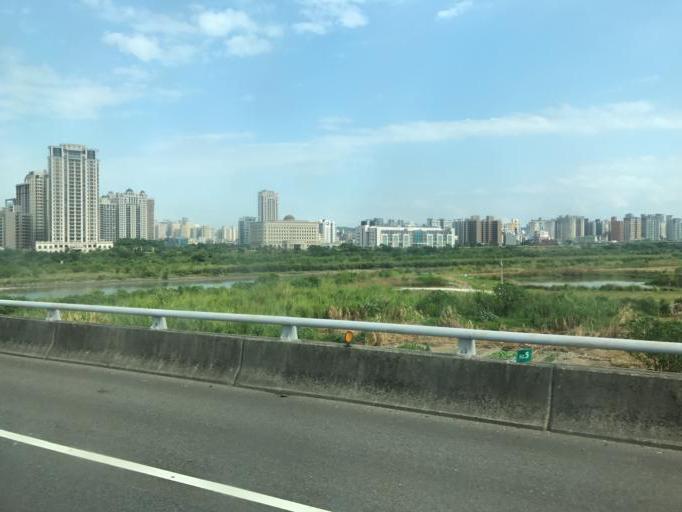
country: TW
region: Taiwan
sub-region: Hsinchu
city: Zhubei
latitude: 24.8112
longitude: 121.0112
